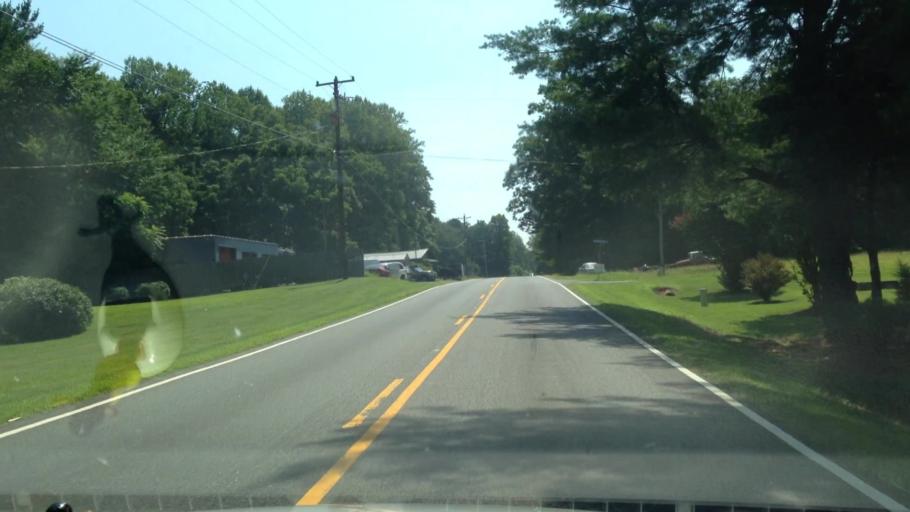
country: US
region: Virginia
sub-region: Patrick County
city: Stuart
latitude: 36.5809
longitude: -80.2723
